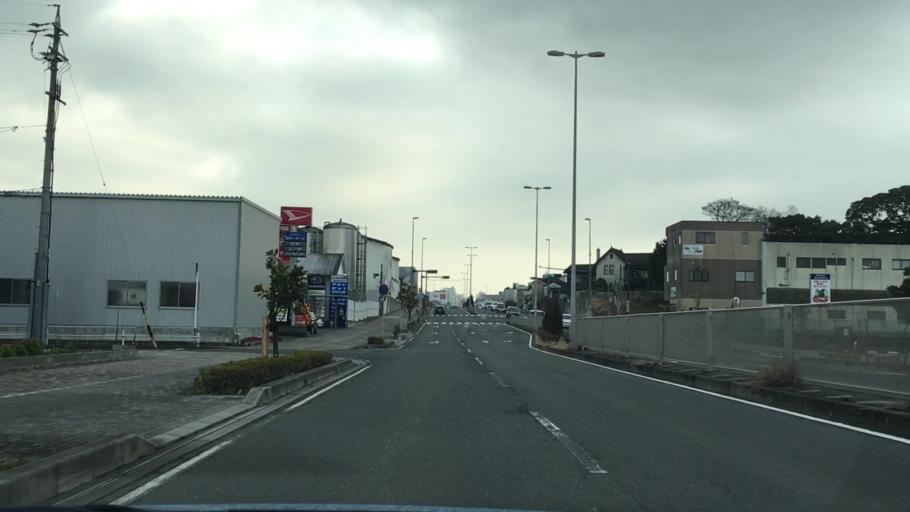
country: JP
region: Aichi
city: Toyohashi
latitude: 34.7675
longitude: 137.3762
